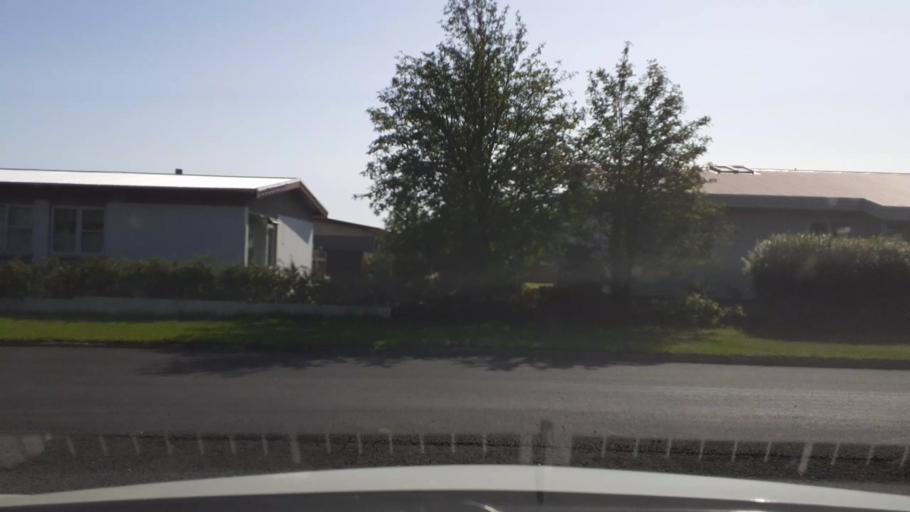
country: IS
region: South
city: Hveragerdi
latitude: 64.0039
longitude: -21.2029
